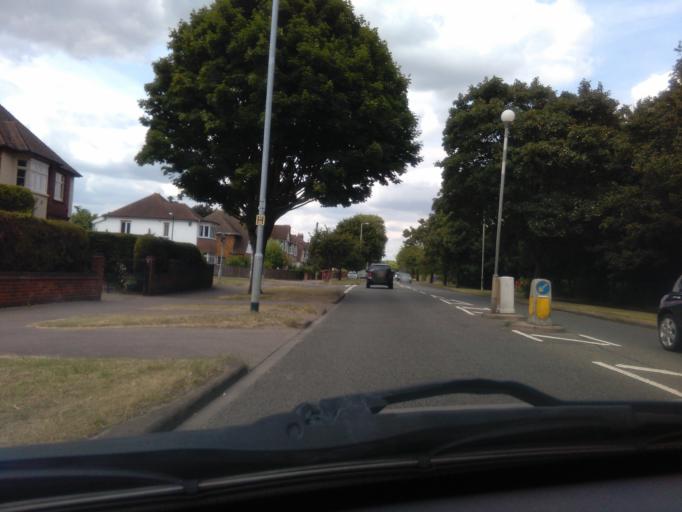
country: GB
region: England
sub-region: Bedford
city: Bedford
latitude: 52.1357
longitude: -0.4453
